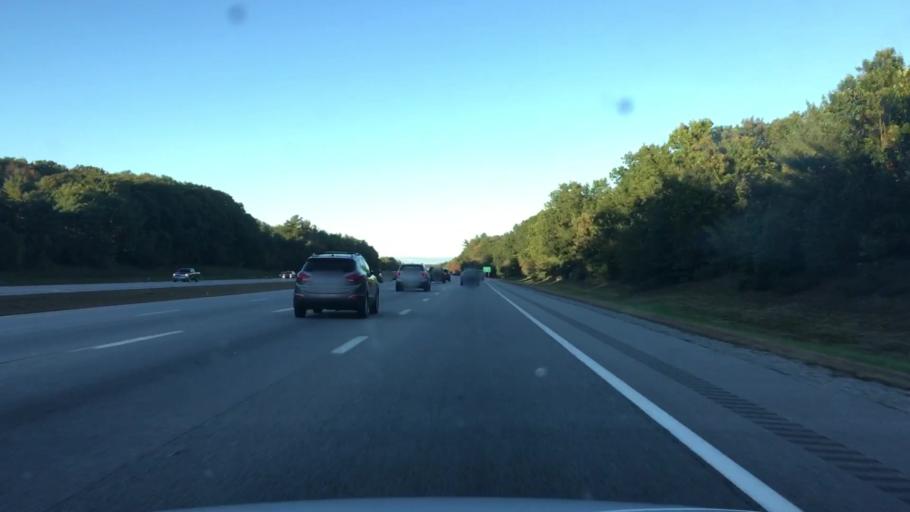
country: US
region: New Hampshire
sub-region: Rockingham County
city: Greenland
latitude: 43.0223
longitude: -70.8287
